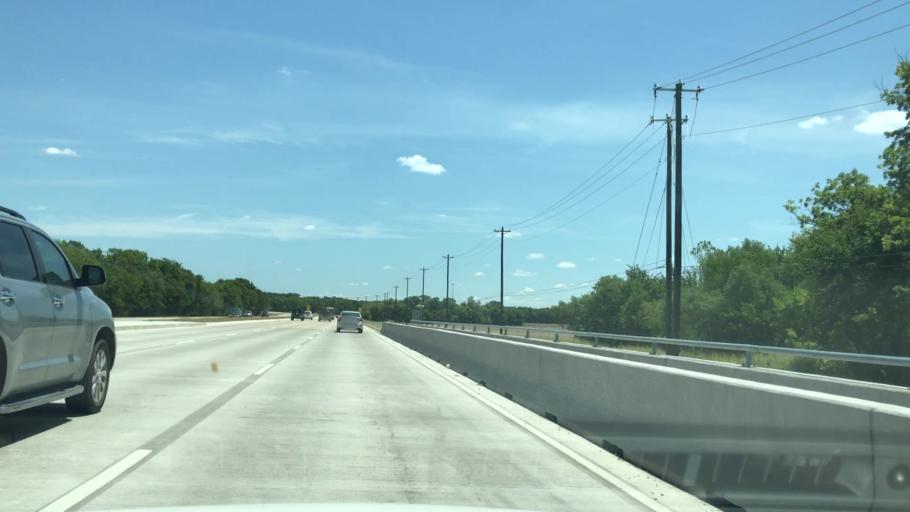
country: US
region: Texas
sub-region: Collin County
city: Lavon
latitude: 33.0233
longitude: -96.4758
